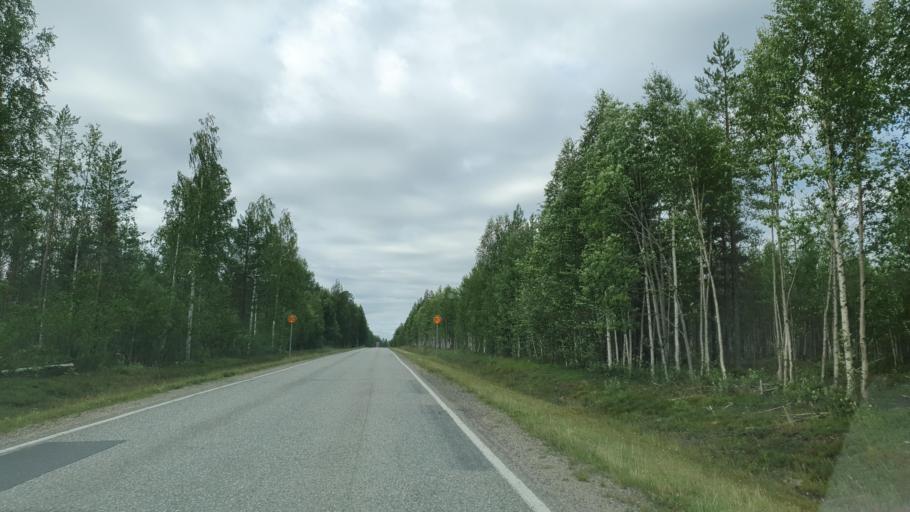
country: FI
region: Lapland
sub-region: Tunturi-Lappi
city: Kittilae
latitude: 67.6101
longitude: 25.2906
